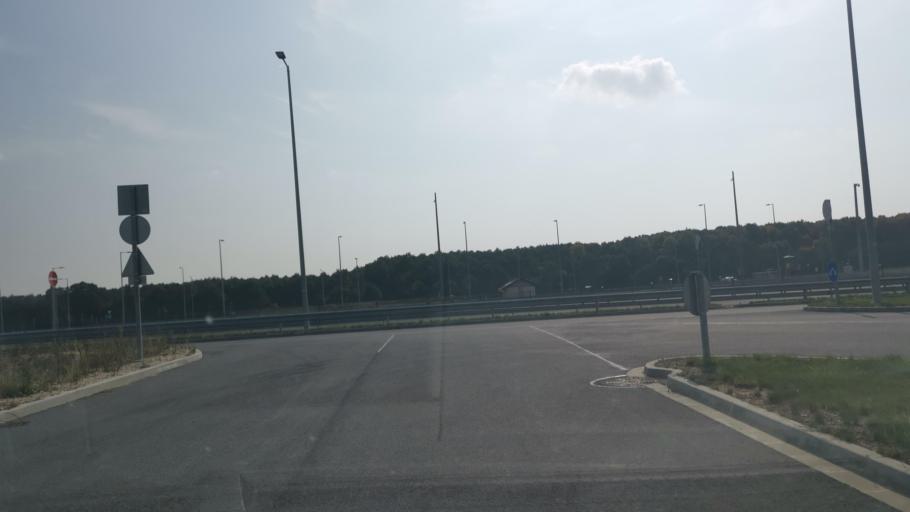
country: HU
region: Gyor-Moson-Sopron
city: Mihalyi
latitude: 47.5639
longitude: 17.0860
